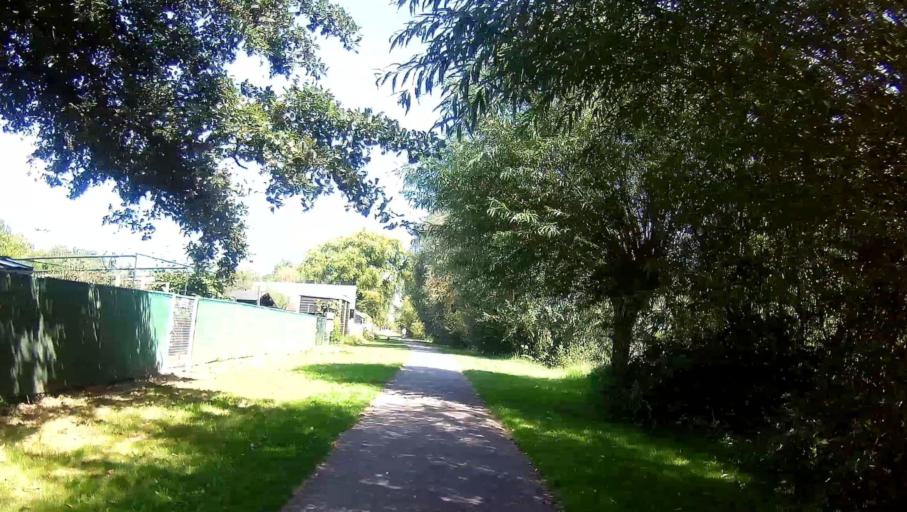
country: NL
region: South Holland
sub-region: Gemeente Ridderkerk
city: Ridderkerk
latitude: 51.8798
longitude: 4.6110
